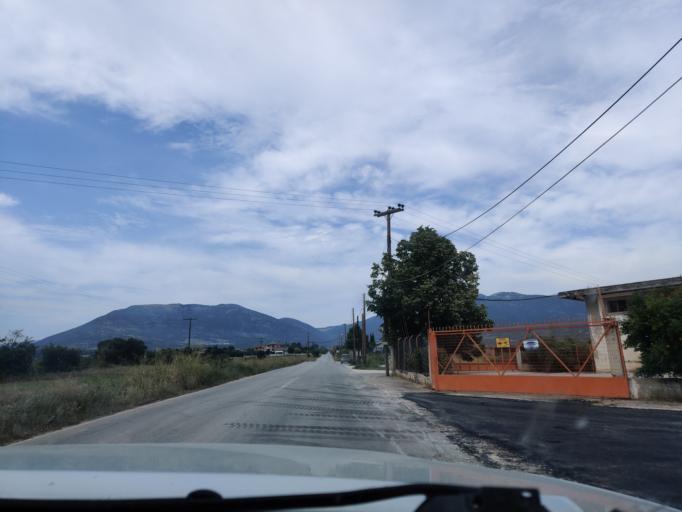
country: GR
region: East Macedonia and Thrace
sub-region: Nomos Dramas
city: Kallifytos
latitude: 41.1586
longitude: 24.2009
